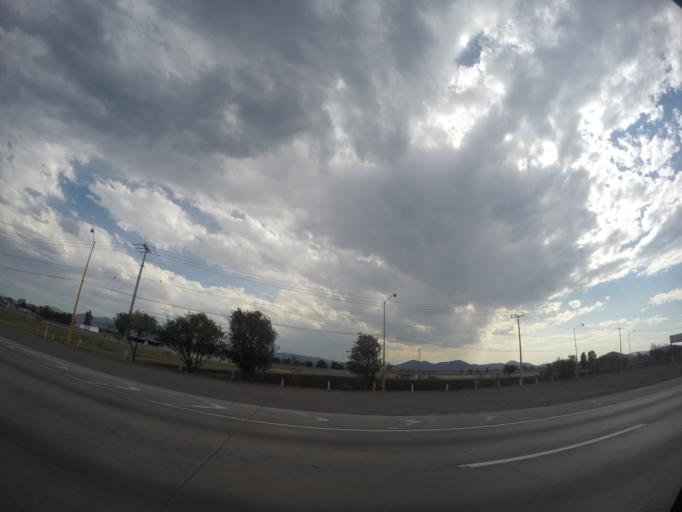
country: MX
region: Queretaro
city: La Estancia
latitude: 20.4139
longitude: -100.0418
